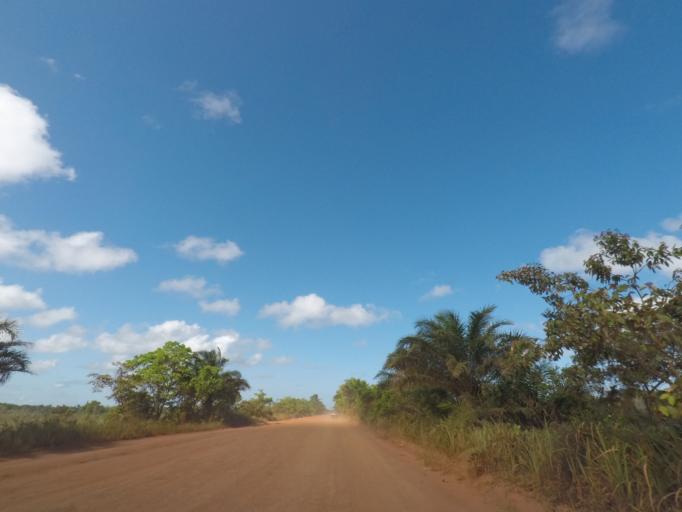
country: BR
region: Bahia
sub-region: Marau
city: Marau
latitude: -14.1583
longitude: -39.0105
